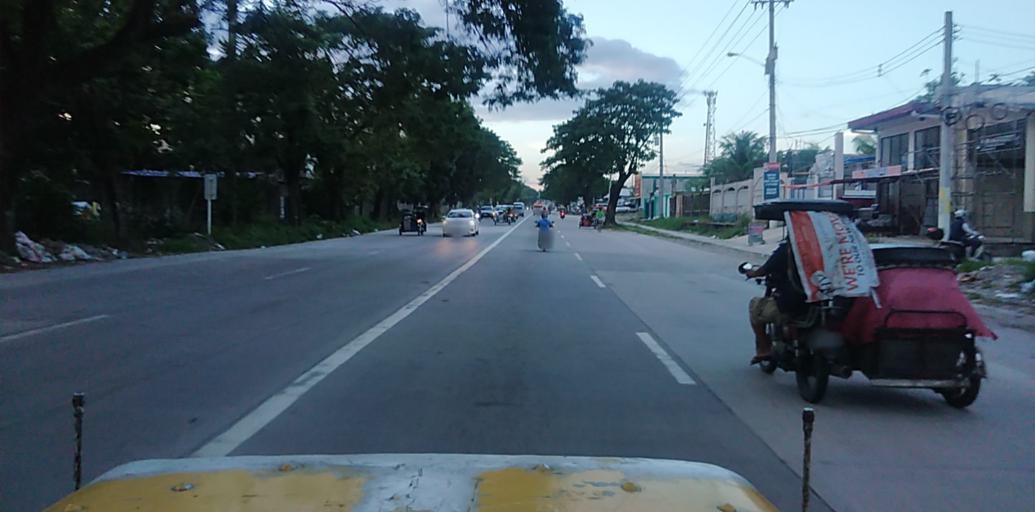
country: PH
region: Central Luzon
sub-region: Province of Pampanga
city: Angeles City
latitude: 15.1275
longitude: 120.5783
